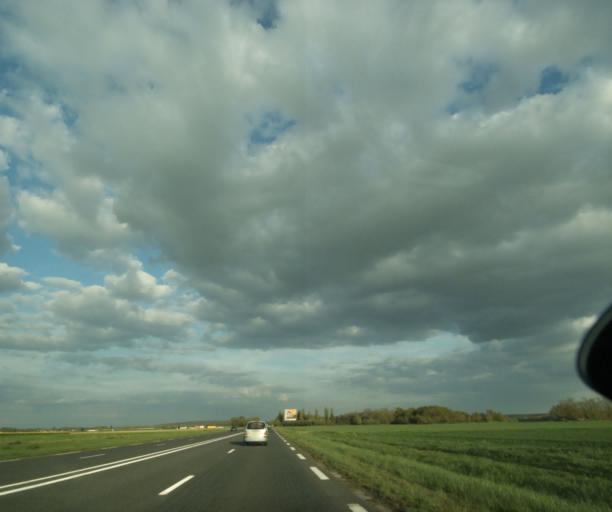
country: FR
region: Ile-de-France
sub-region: Departement de Seine-et-Marne
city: Perthes
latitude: 48.4599
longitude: 2.5740
